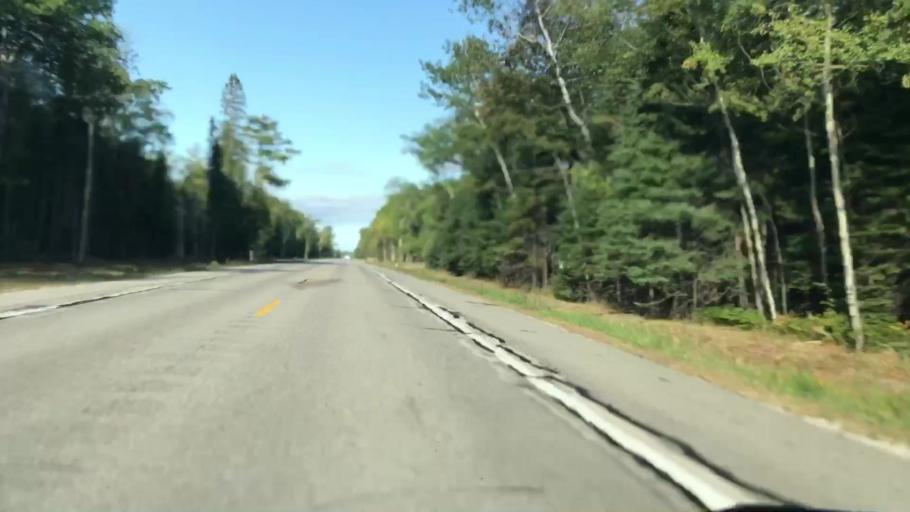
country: US
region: Michigan
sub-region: Luce County
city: Newberry
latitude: 46.3035
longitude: -85.3527
